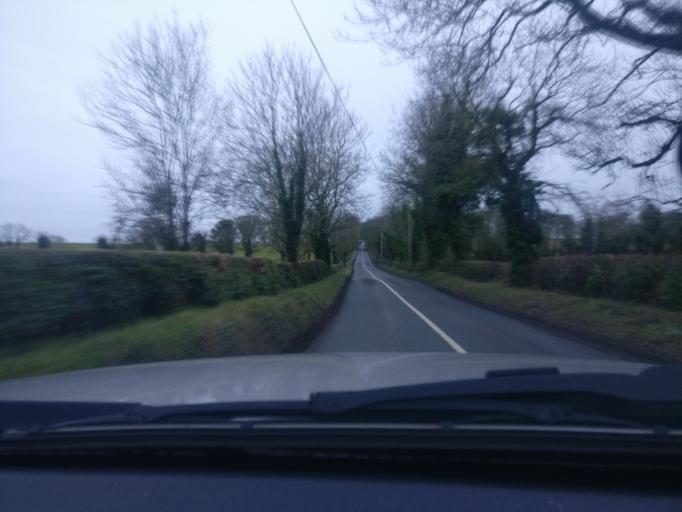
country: IE
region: Leinster
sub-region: An Mhi
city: Dunshaughlin
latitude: 53.4790
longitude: -6.6174
